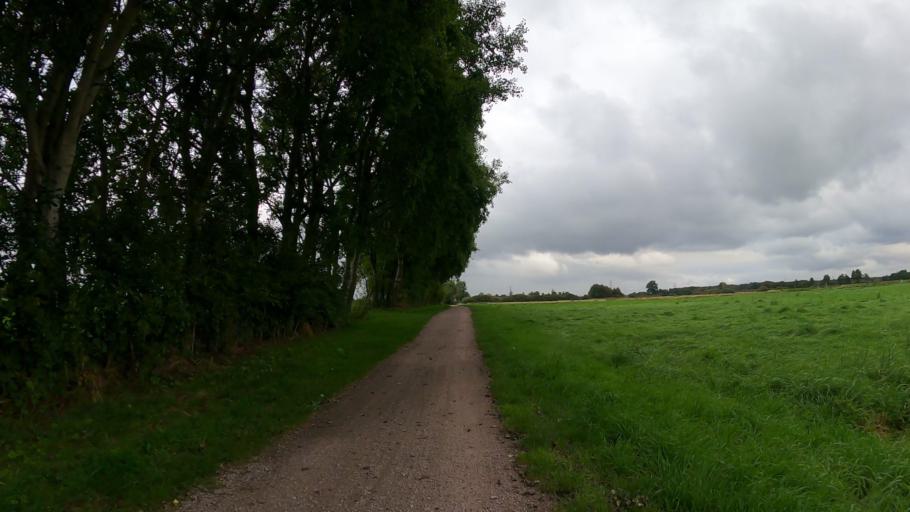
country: DE
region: Lower Saxony
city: Neu Wulmstorf
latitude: 53.4746
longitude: 9.7735
